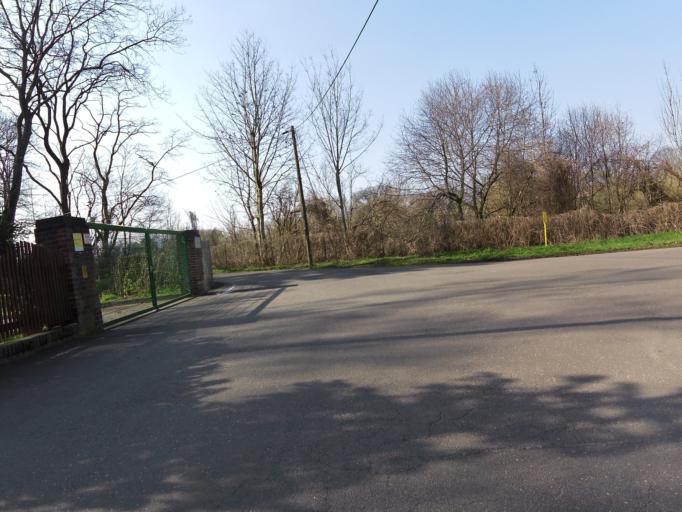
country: DE
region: Saxony
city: Leipzig
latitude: 51.3734
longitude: 12.3081
